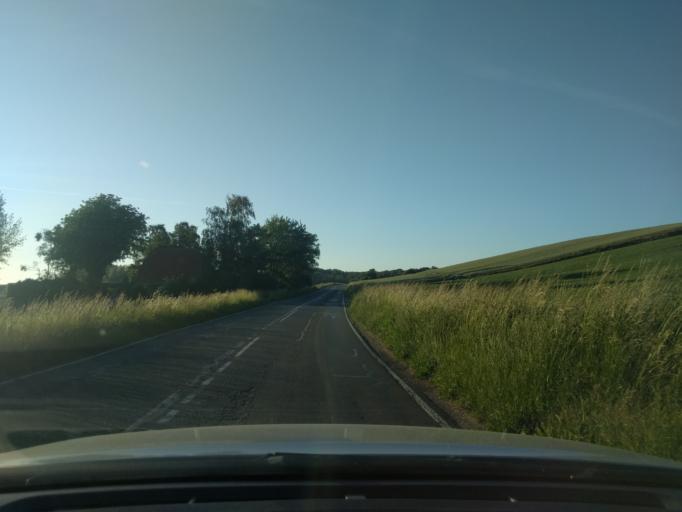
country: DK
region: South Denmark
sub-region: Kerteminde Kommune
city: Kerteminde
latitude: 55.5232
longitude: 10.6537
